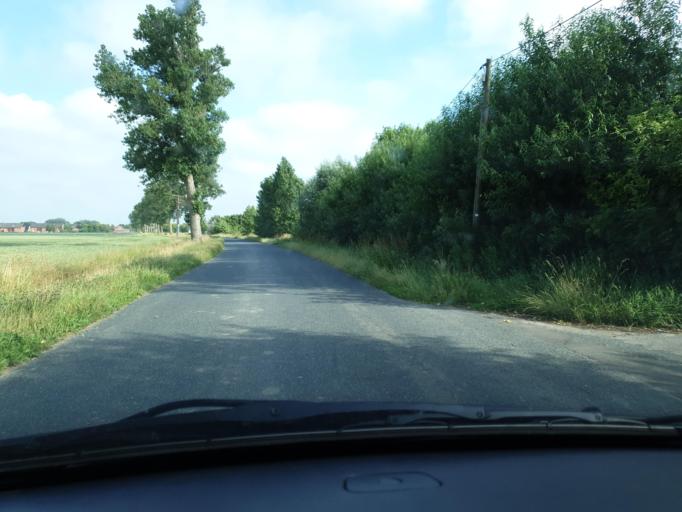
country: DE
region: Schleswig-Holstein
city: Friedrichskoog
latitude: 54.0096
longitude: 8.8666
